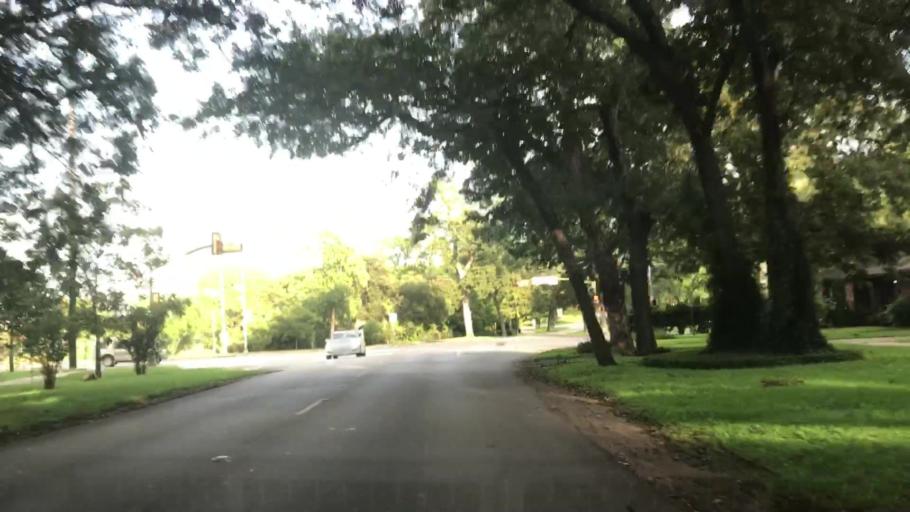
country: US
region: Texas
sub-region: Dallas County
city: Dallas
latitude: 32.7667
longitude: -96.8364
